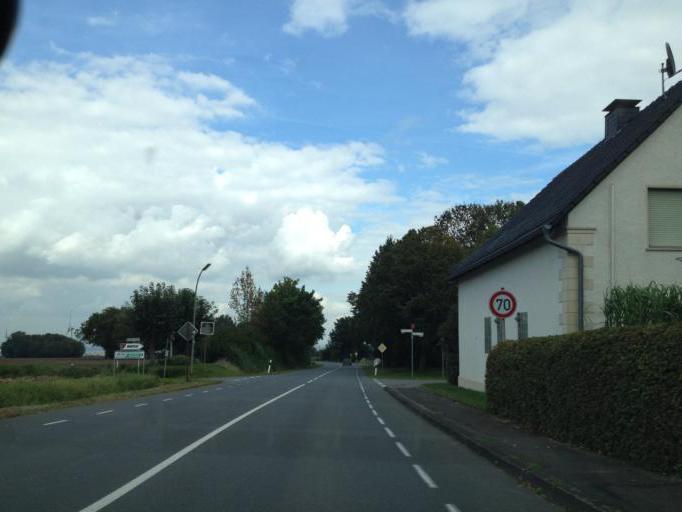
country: DE
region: North Rhine-Westphalia
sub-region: Regierungsbezirk Arnsberg
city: Mohnesee
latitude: 51.5094
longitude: 8.0681
